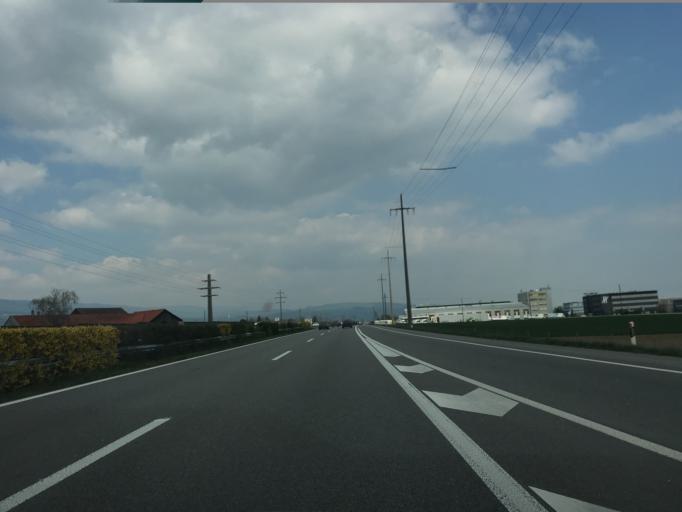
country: CH
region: Vaud
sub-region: Nyon District
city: Trelex
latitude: 46.3969
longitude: 6.2110
